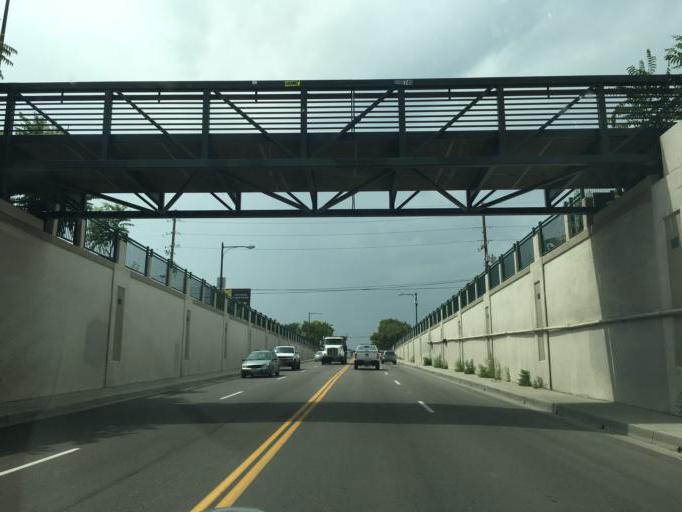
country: US
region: Colorado
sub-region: Denver County
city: Denver
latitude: 39.7693
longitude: -104.9978
